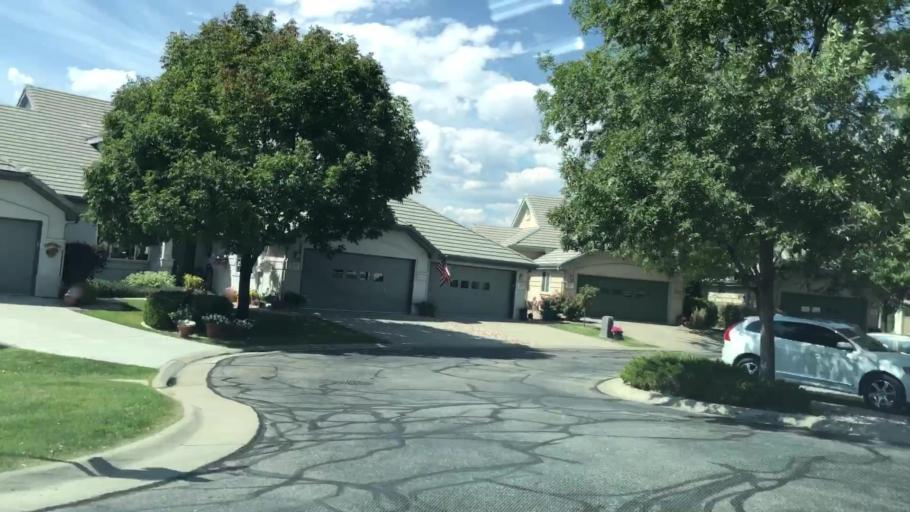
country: US
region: Colorado
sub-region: Larimer County
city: Loveland
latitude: 40.3973
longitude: -105.1423
